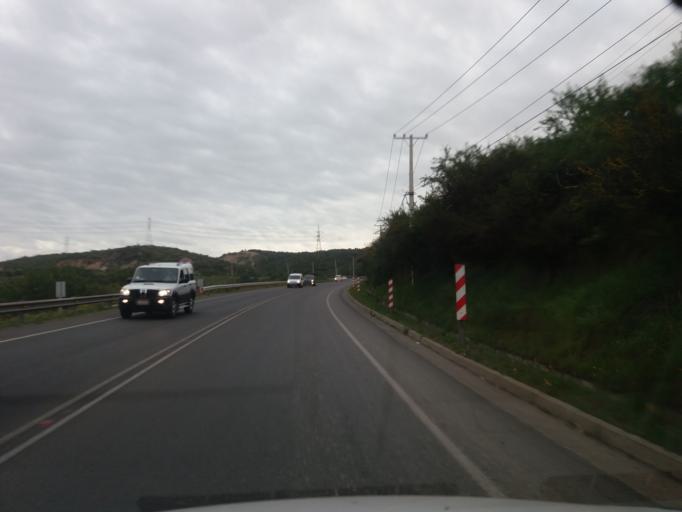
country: CL
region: Valparaiso
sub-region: Provincia de Marga Marga
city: Limache
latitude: -32.9534
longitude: -71.2853
